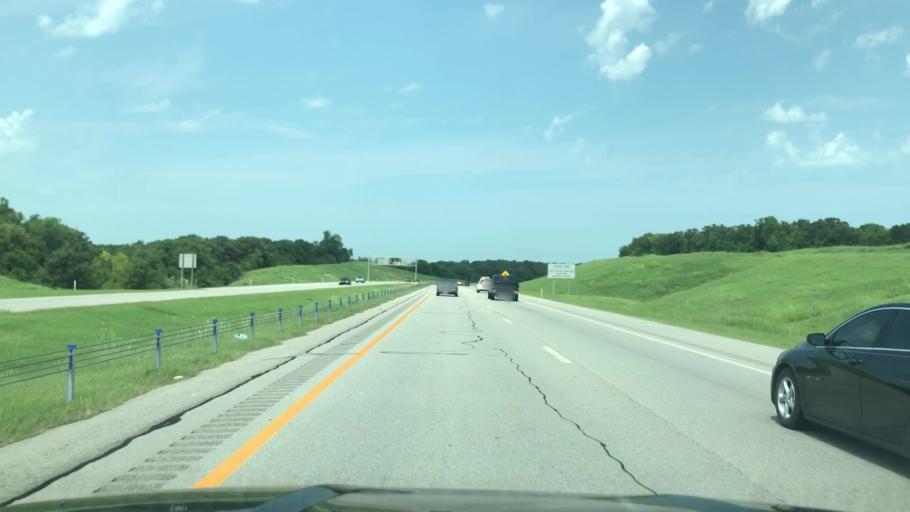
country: US
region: Oklahoma
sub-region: Rogers County
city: Catoosa
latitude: 36.1787
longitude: -95.7319
